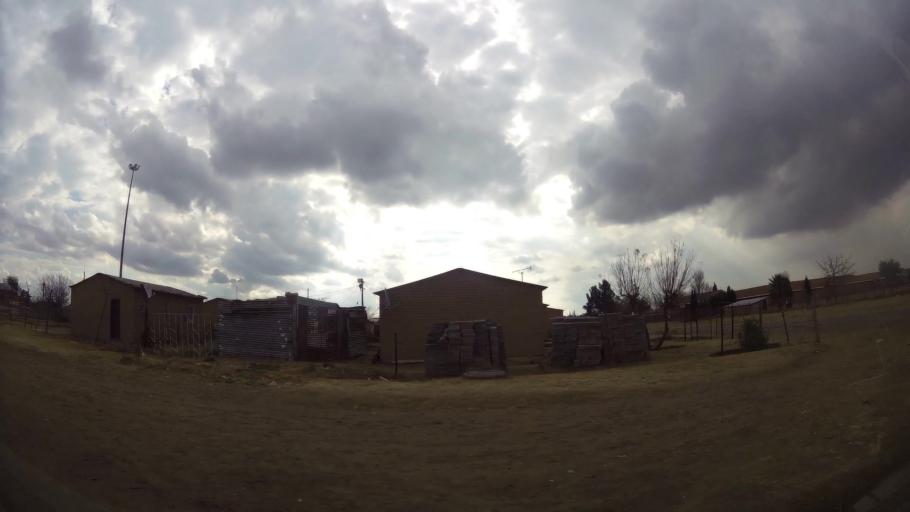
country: ZA
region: Orange Free State
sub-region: Fezile Dabi District Municipality
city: Sasolburg
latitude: -26.8541
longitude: 27.8548
